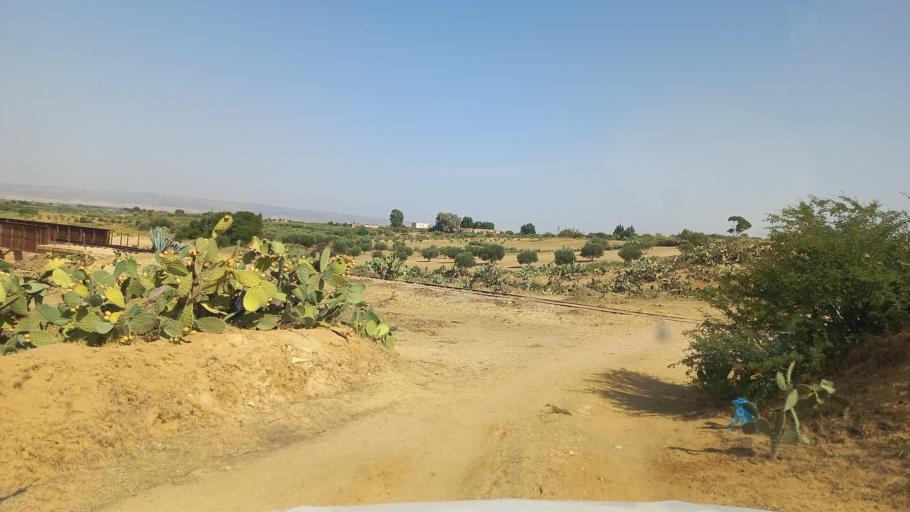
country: TN
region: Al Qasrayn
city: Kasserine
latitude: 35.2275
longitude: 9.0494
